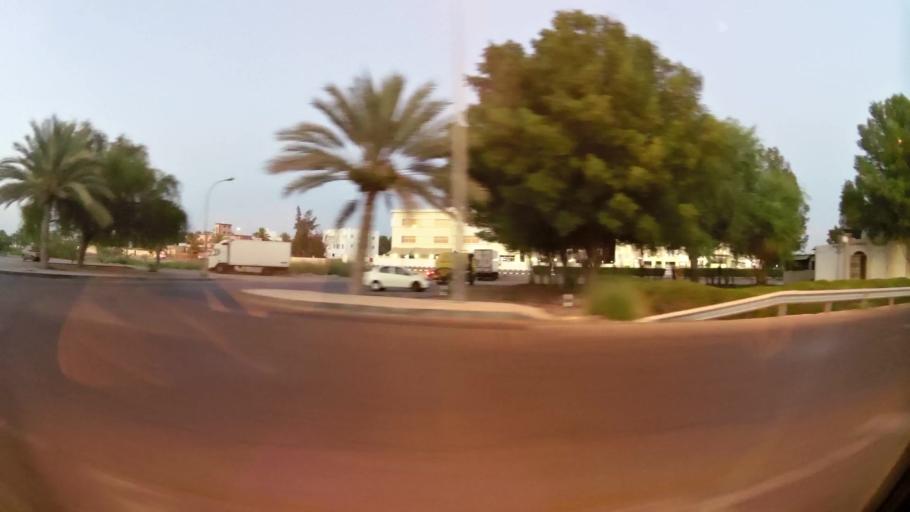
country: OM
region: Muhafazat Masqat
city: As Sib al Jadidah
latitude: 23.6746
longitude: 58.1919
